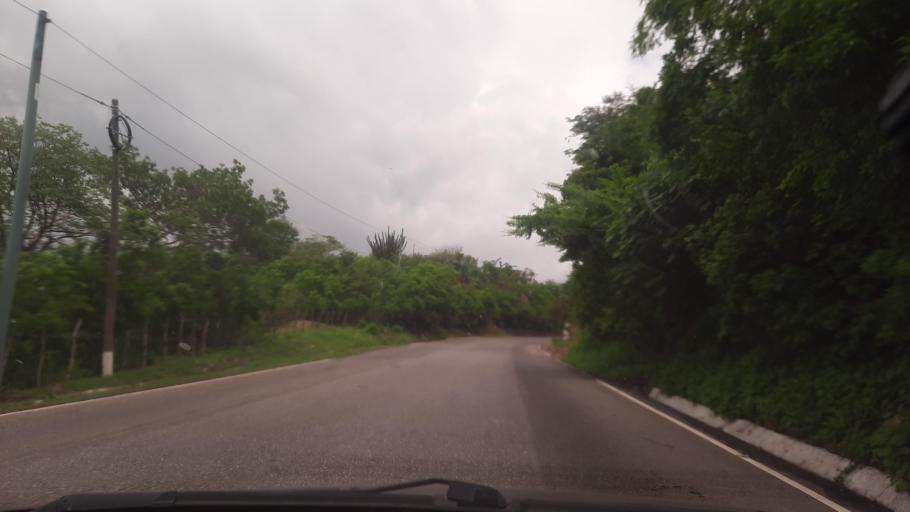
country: GT
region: Chiquimula
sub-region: Municipio de Chiquimula
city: Chiquimula
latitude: 14.8765
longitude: -89.5137
